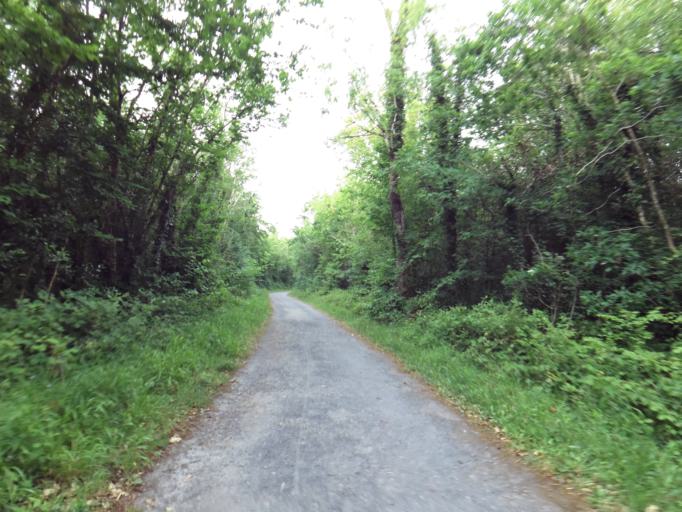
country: IE
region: Connaught
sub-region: County Galway
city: Gort
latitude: 53.0800
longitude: -8.8686
